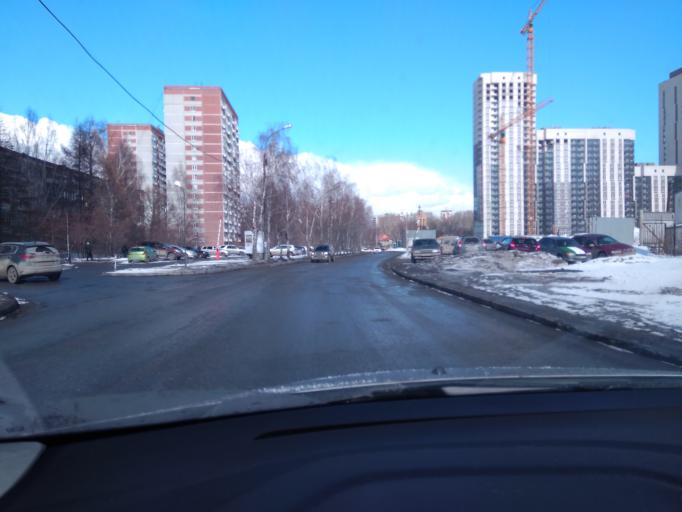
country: RU
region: Sverdlovsk
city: Sovkhoznyy
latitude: 56.8122
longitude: 60.5673
